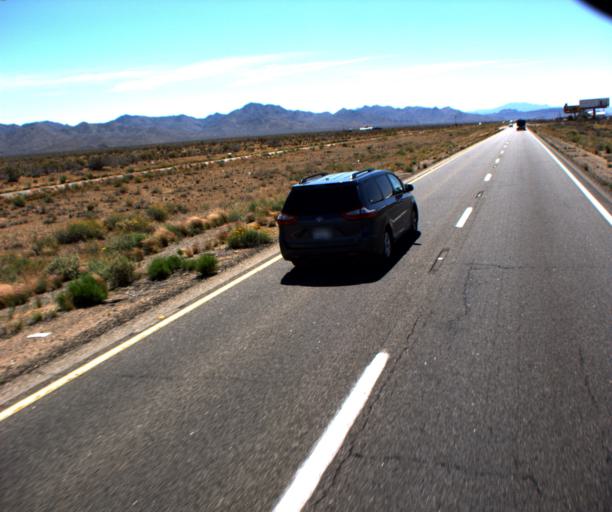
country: US
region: Arizona
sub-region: Mohave County
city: Golden Valley
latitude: 35.3396
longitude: -114.2181
